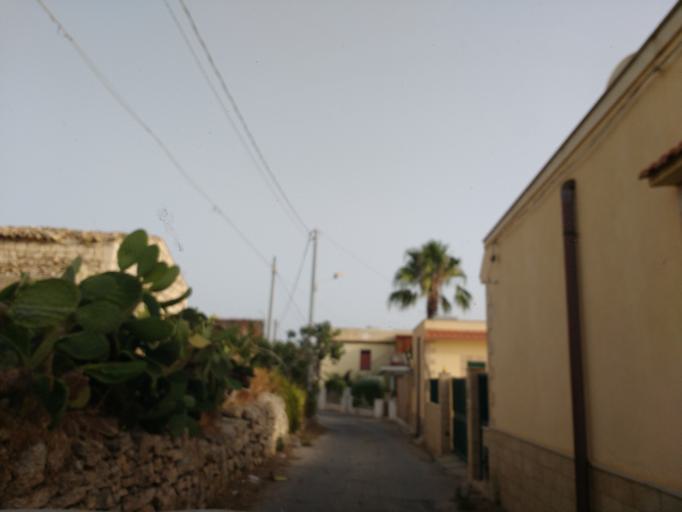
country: IT
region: Sicily
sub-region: Ragusa
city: Cava d'Aliga
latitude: 36.7312
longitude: 14.6904
